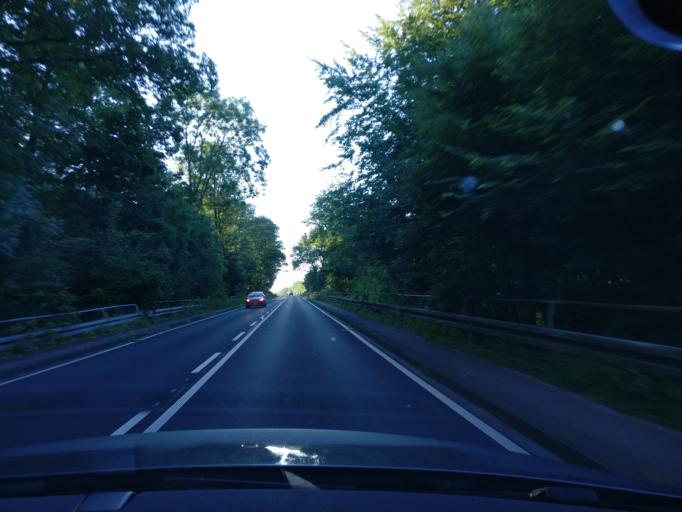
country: DE
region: North Rhine-Westphalia
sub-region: Regierungsbezirk Dusseldorf
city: Ratingen
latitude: 51.3056
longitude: 6.7821
